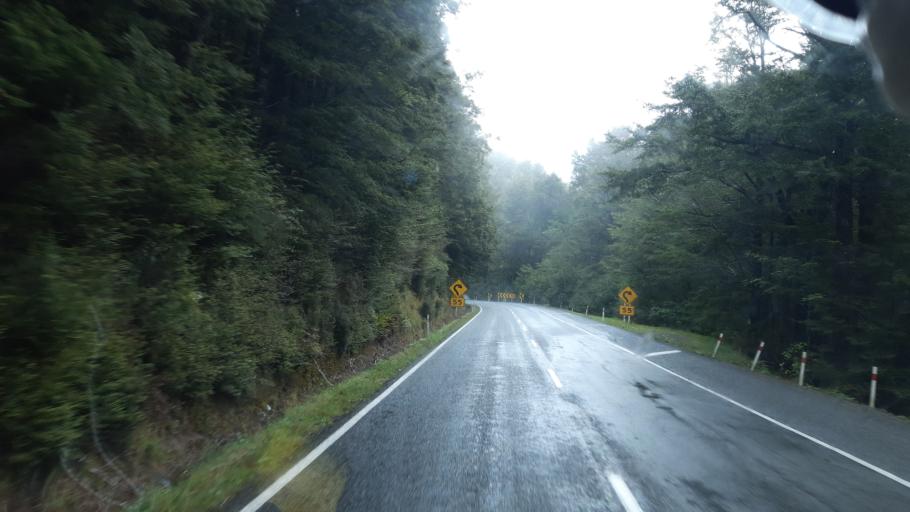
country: NZ
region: Canterbury
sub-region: Hurunui District
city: Amberley
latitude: -42.3794
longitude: 172.3407
